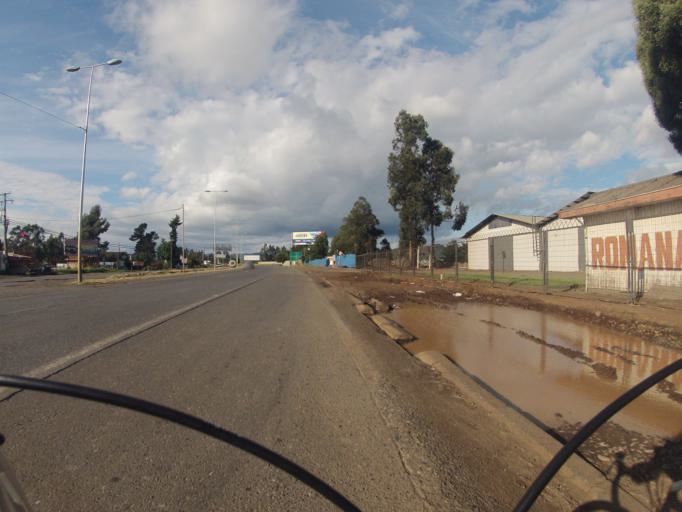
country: CL
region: Araucania
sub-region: Provincia de Cautin
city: Temuco
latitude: -38.7769
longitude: -72.6082
